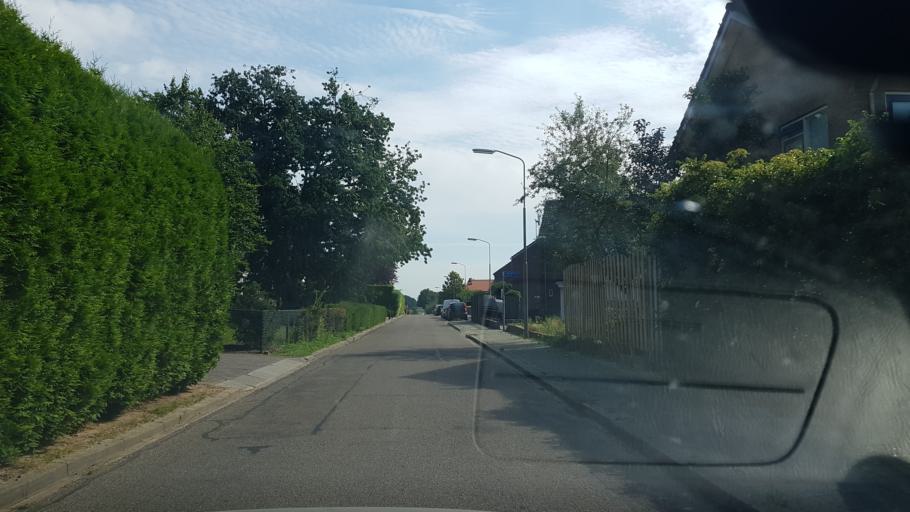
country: NL
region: Gelderland
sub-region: Gemeente Groesbeek
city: Bredeweg
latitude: 51.7601
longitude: 5.9373
